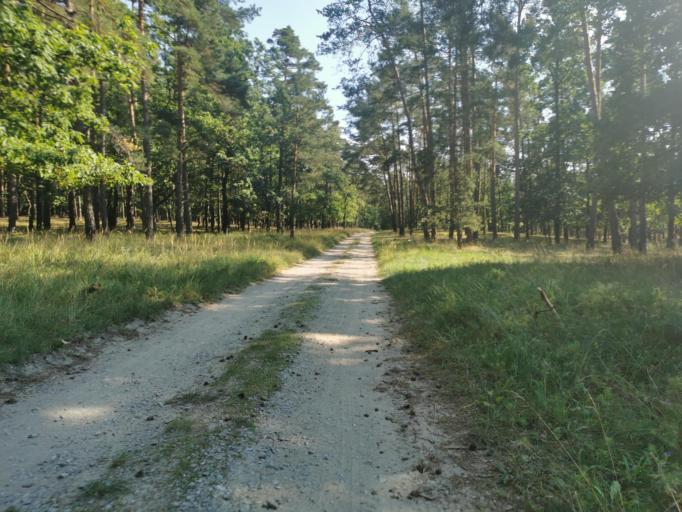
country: SK
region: Trnavsky
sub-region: Okres Senica
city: Senica
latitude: 48.6410
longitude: 17.2767
